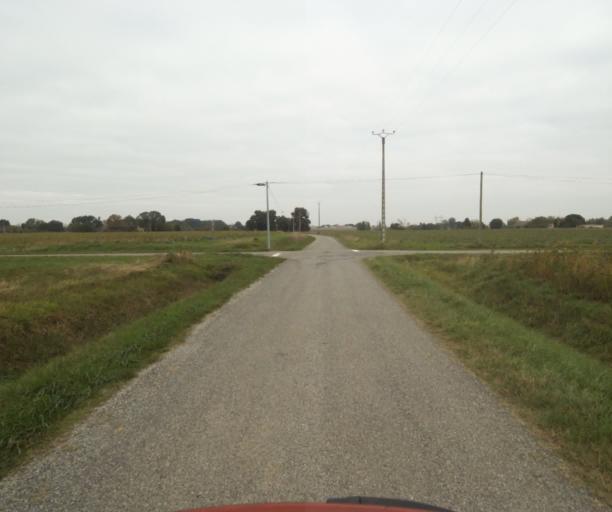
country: FR
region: Midi-Pyrenees
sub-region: Departement du Tarn-et-Garonne
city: Verdun-sur-Garonne
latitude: 43.7983
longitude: 1.2359
